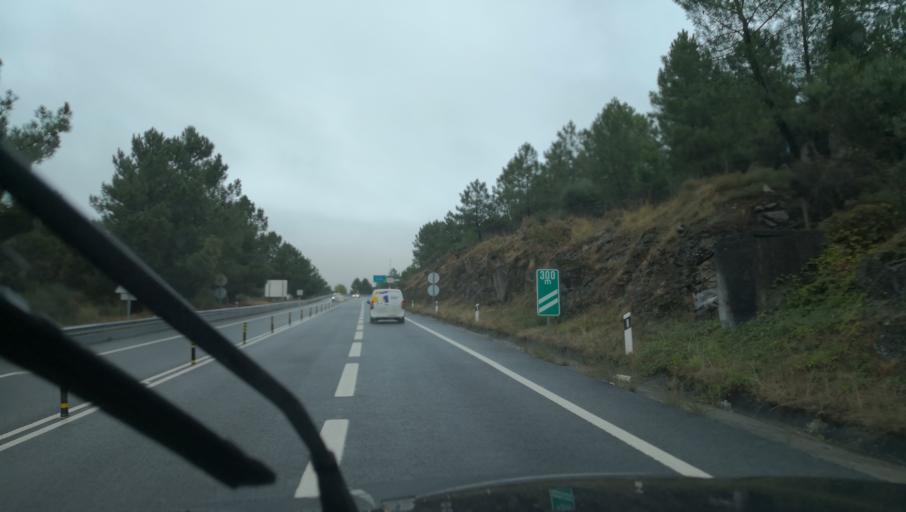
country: PT
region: Vila Real
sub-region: Vila Real
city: Vila Real
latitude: 41.3272
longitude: -7.6788
